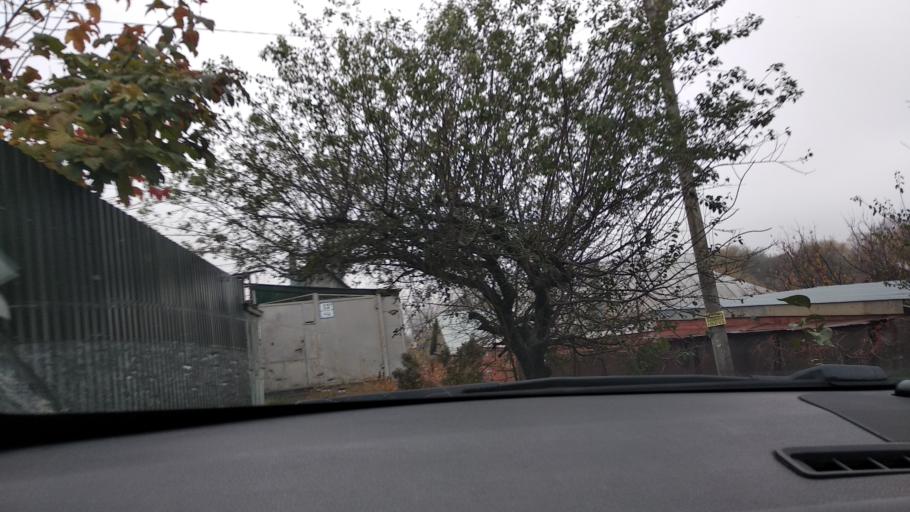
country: RU
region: Krasnodarskiy
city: Krasnodar
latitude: 45.0040
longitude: 39.0172
